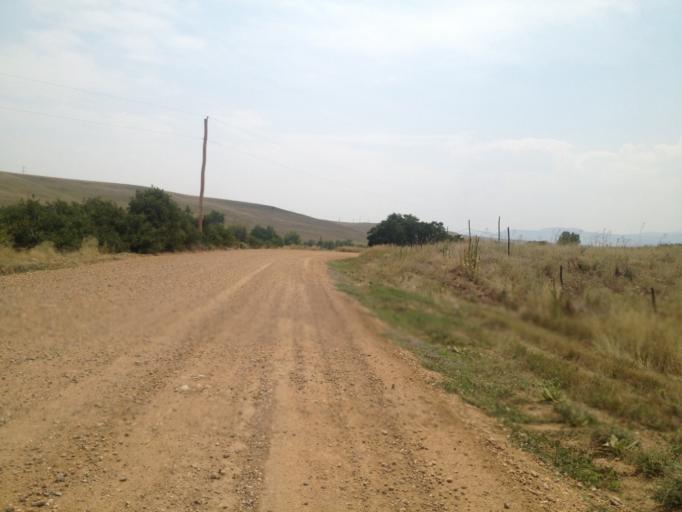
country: US
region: Colorado
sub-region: Boulder County
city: Superior
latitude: 39.9451
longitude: -105.1871
